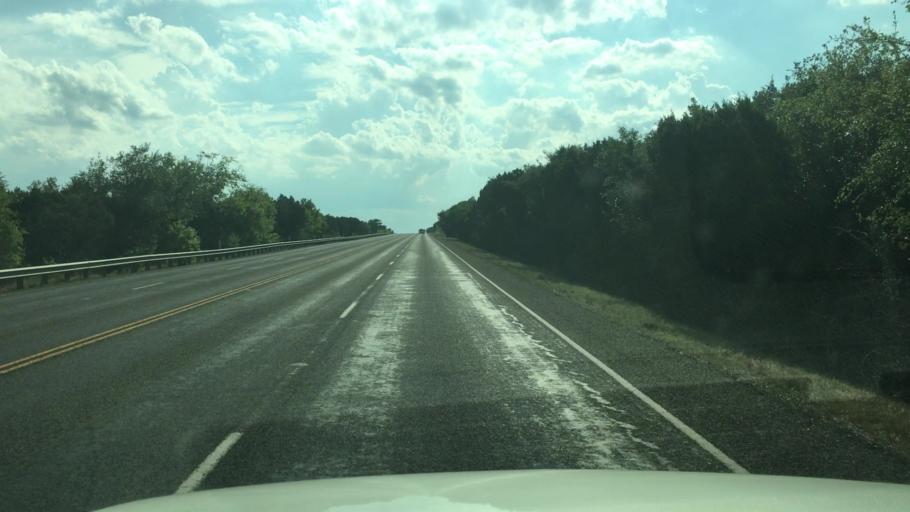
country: US
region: Texas
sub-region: Blanco County
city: Johnson City
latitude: 30.2096
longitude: -98.2929
